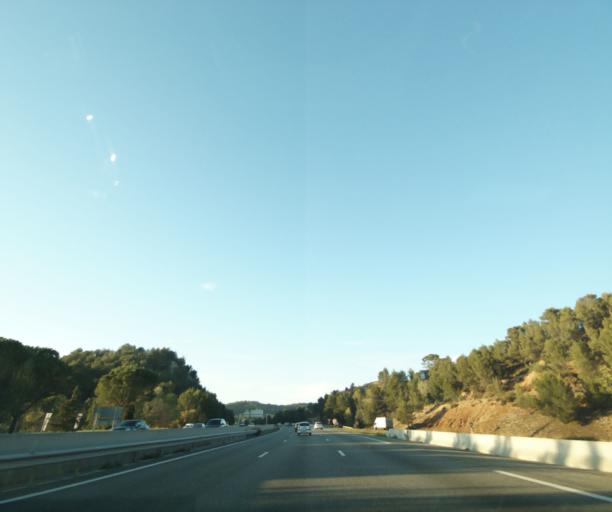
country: FR
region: Provence-Alpes-Cote d'Azur
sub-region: Departement des Bouches-du-Rhone
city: Le Tholonet
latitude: 43.4969
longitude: 5.5248
